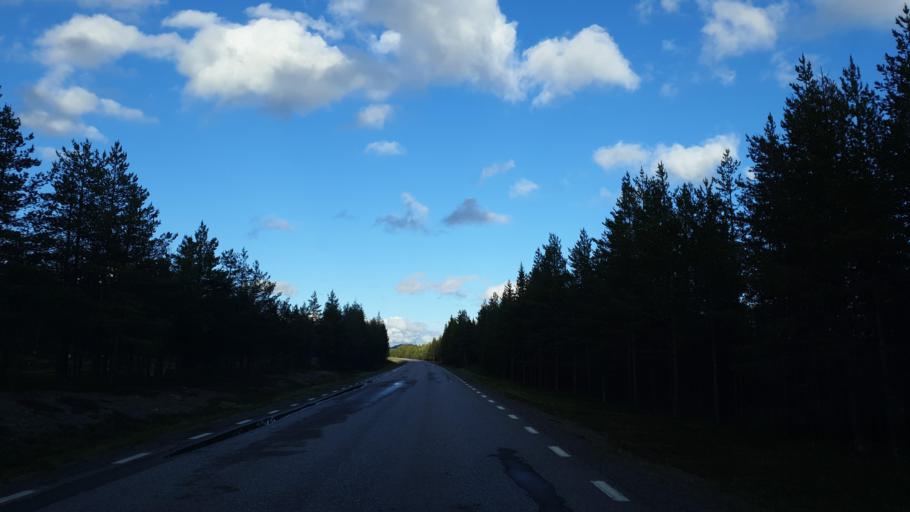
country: SE
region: Norrbotten
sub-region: Arvidsjaurs Kommun
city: Arvidsjaur
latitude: 65.7340
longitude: 18.6349
